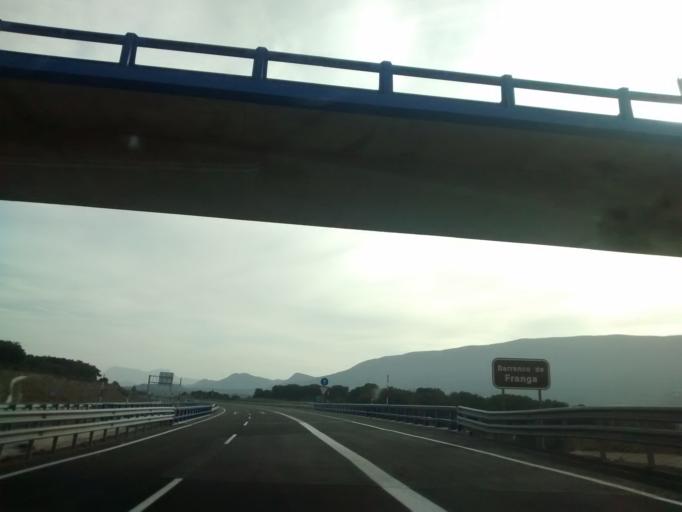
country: ES
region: Aragon
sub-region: Provincia de Zaragoza
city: Siguees
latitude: 42.6147
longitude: -0.9979
